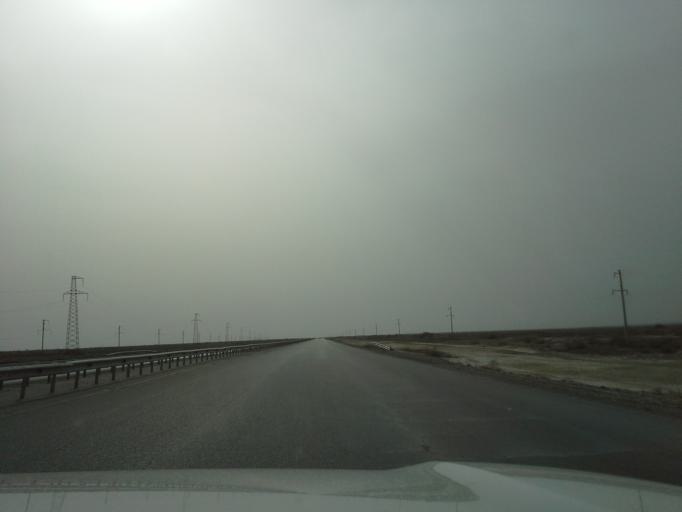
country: TM
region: Ahal
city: Kaka
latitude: 37.5183
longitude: 59.4321
